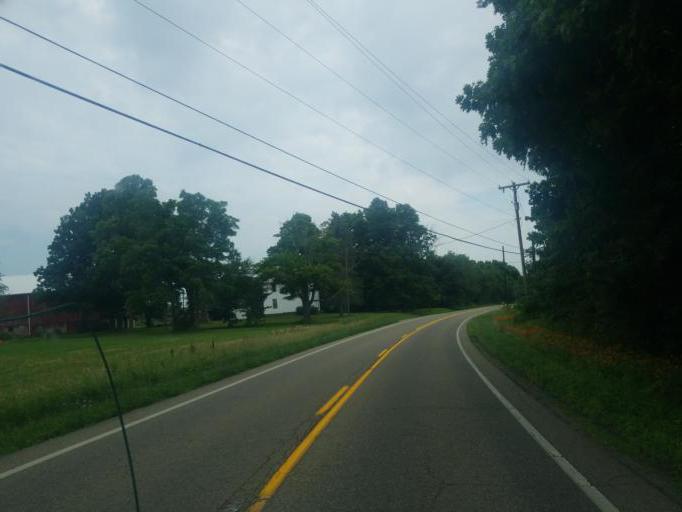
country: US
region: Ohio
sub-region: Columbiana County
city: Salem
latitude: 40.7877
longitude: -80.9278
